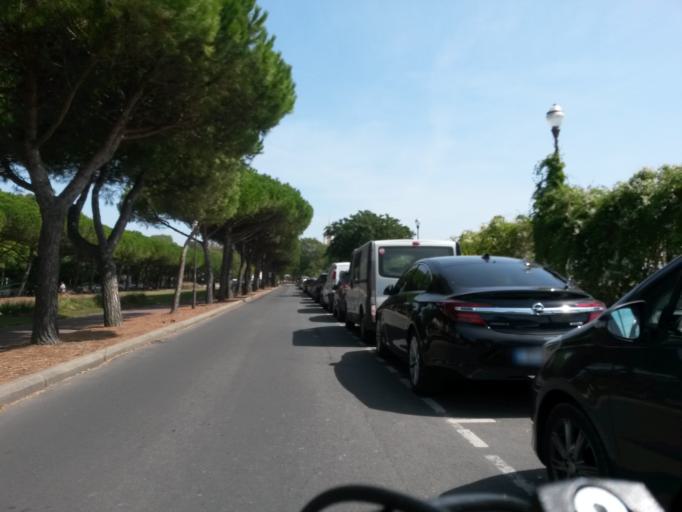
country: FR
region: Poitou-Charentes
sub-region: Departement de la Charente-Maritime
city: La Rochelle
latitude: 46.1558
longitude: -1.1632
